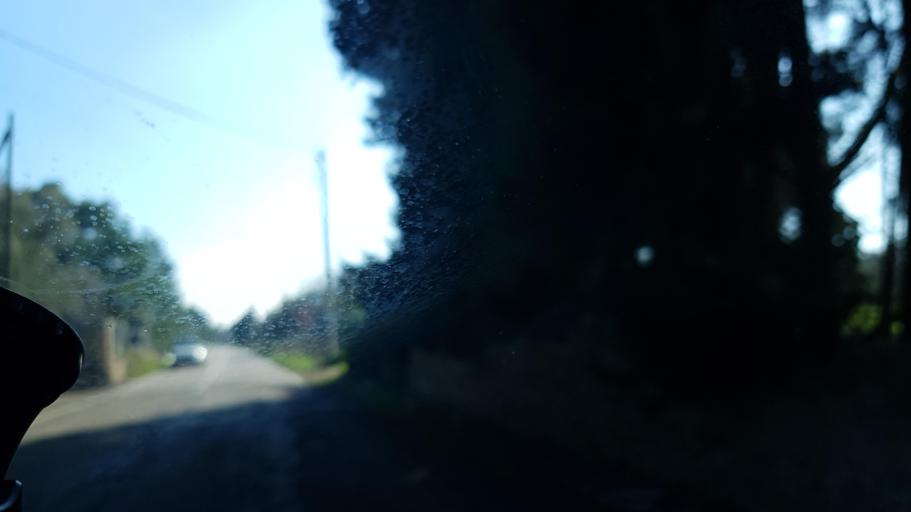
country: IT
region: Apulia
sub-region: Provincia di Lecce
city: Novoli
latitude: 40.3637
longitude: 18.0717
